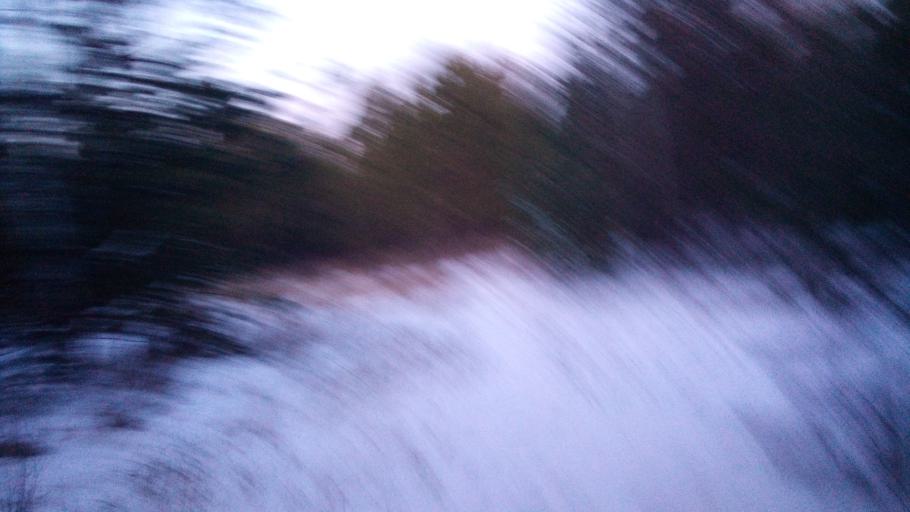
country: RU
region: Chelyabinsk
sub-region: Gorod Chelyabinsk
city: Chelyabinsk
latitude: 55.1621
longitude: 61.3331
